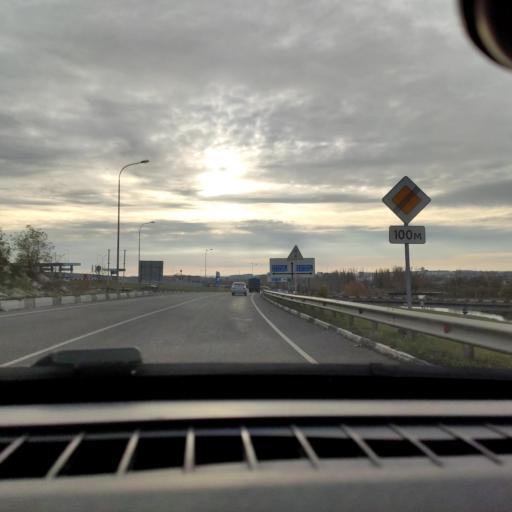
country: RU
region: Belgorod
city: Alekseyevka
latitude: 50.6403
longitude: 38.6662
